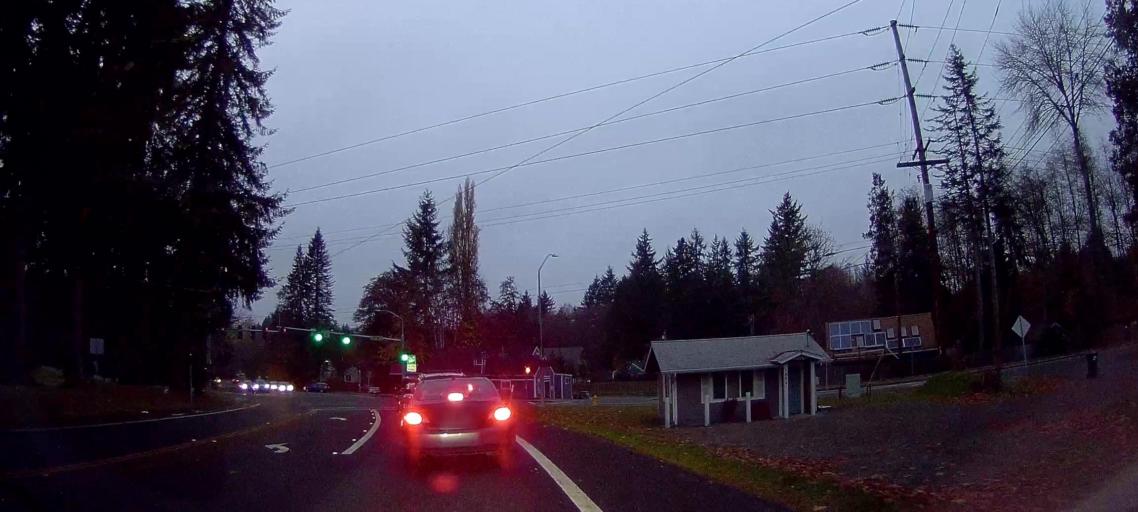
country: US
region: Washington
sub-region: Thurston County
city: Olympia
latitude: 47.0323
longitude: -122.8654
